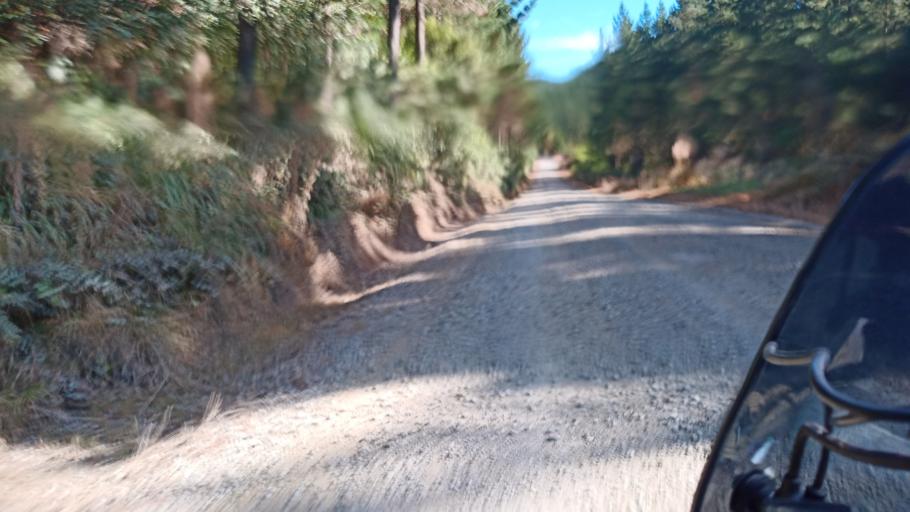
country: NZ
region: Hawke's Bay
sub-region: Wairoa District
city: Wairoa
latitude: -38.9231
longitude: 177.2045
